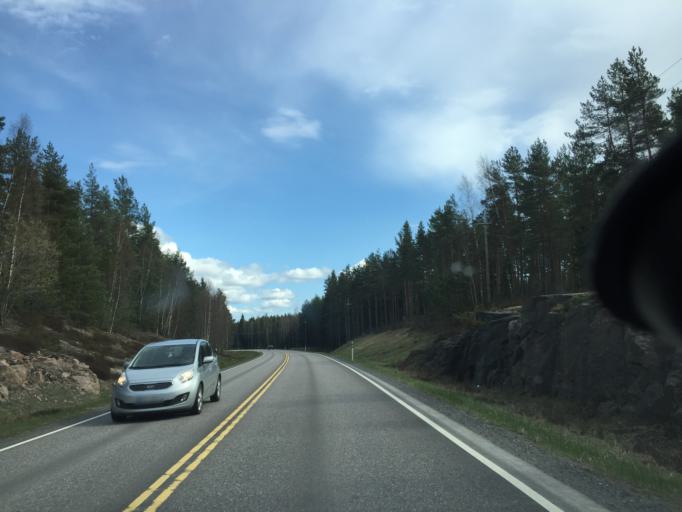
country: FI
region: Uusimaa
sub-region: Raaseporin
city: Ekenaes
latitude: 60.0413
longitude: 23.3417
